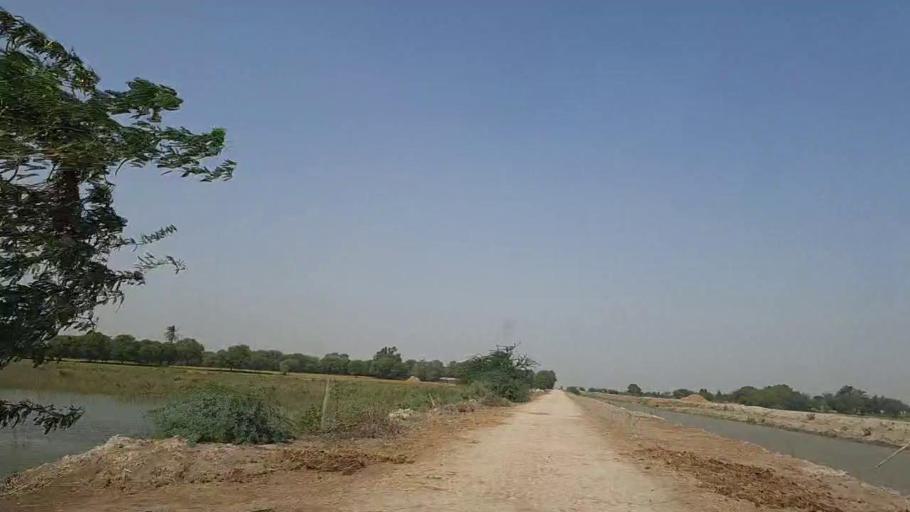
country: PK
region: Sindh
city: Daro Mehar
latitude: 24.7628
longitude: 68.1358
